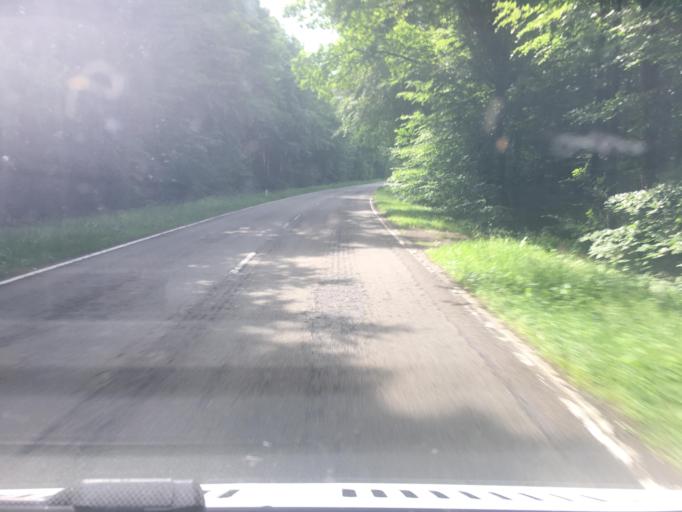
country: BE
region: Wallonia
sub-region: Province du Luxembourg
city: Florenville
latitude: 49.6463
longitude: 5.3408
